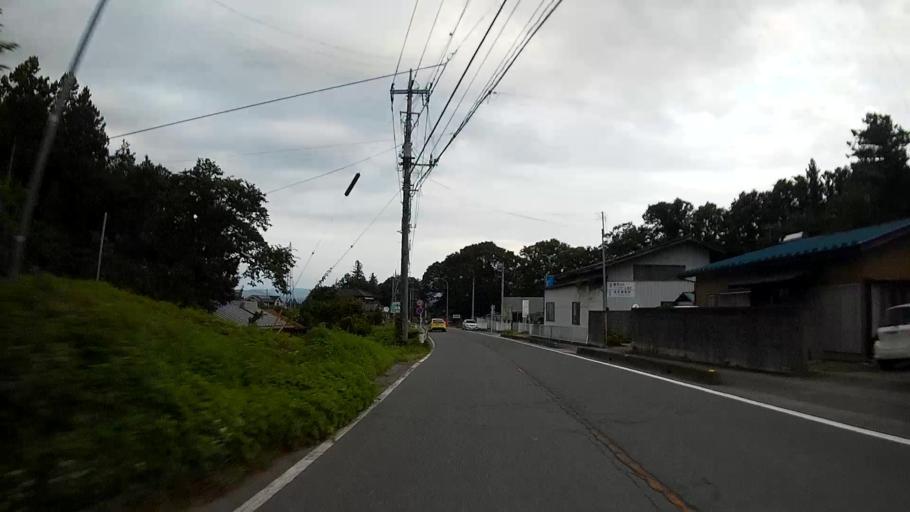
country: JP
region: Saitama
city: Chichibu
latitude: 35.9624
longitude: 139.0514
